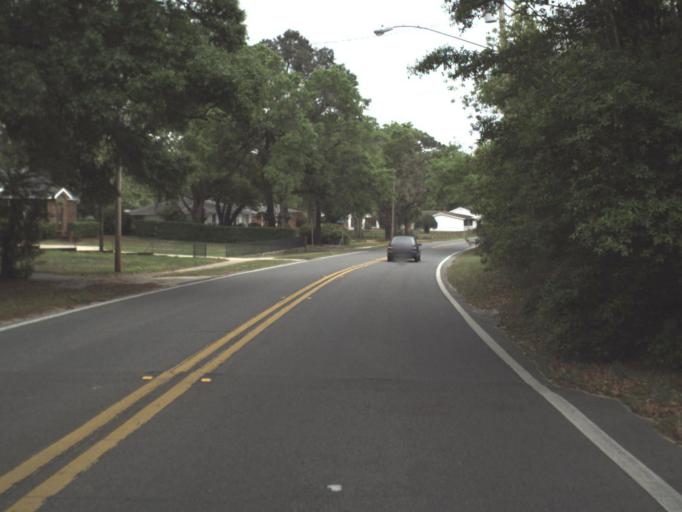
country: US
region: Florida
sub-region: Escambia County
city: East Pensacola Heights
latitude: 30.4350
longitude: -87.1824
